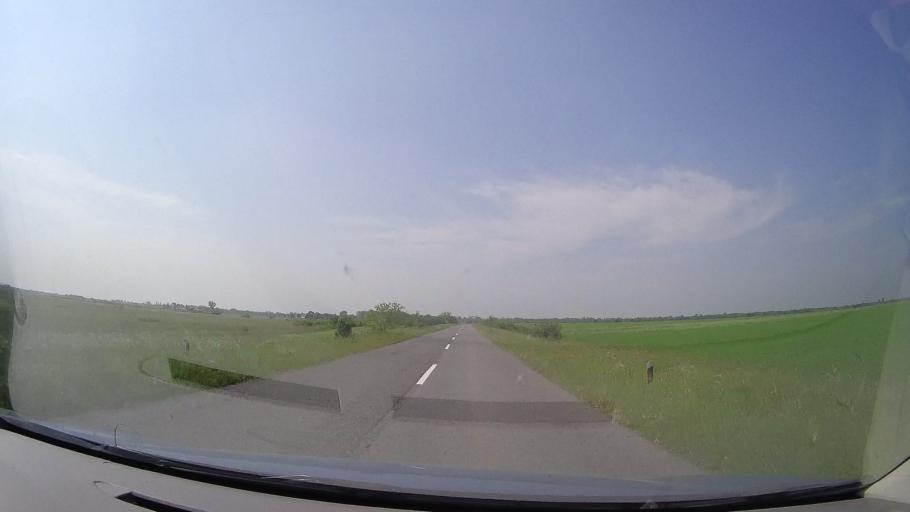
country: RS
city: Jarkovac
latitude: 45.2851
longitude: 20.7636
